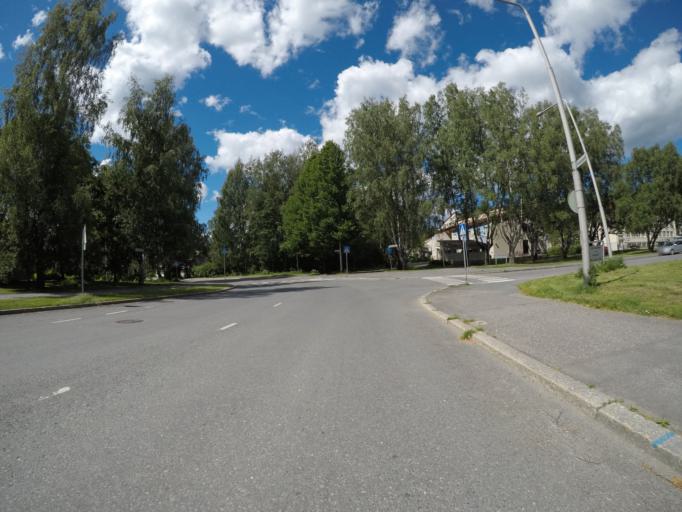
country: FI
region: Haeme
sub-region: Haemeenlinna
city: Haemeenlinna
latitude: 61.0107
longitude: 24.4376
